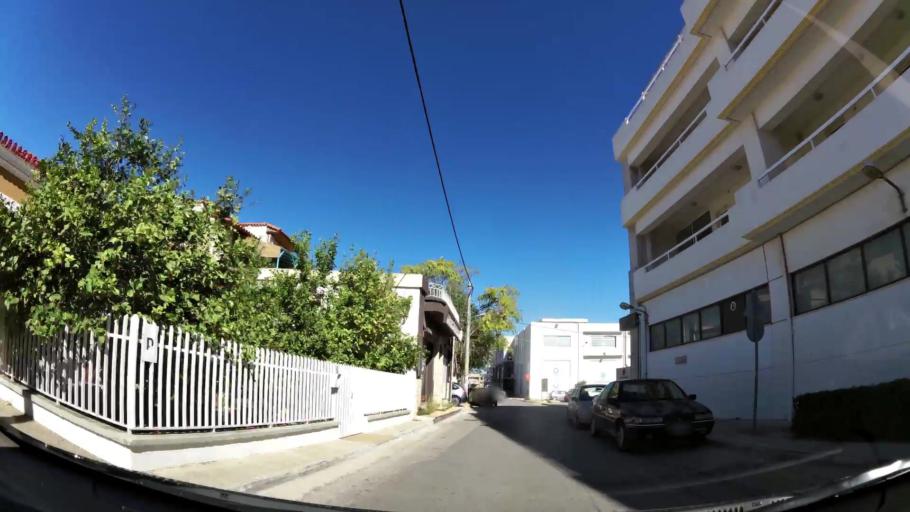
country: GR
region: Attica
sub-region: Nomarchia Anatolikis Attikis
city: Koropi
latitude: 37.9067
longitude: 23.8747
